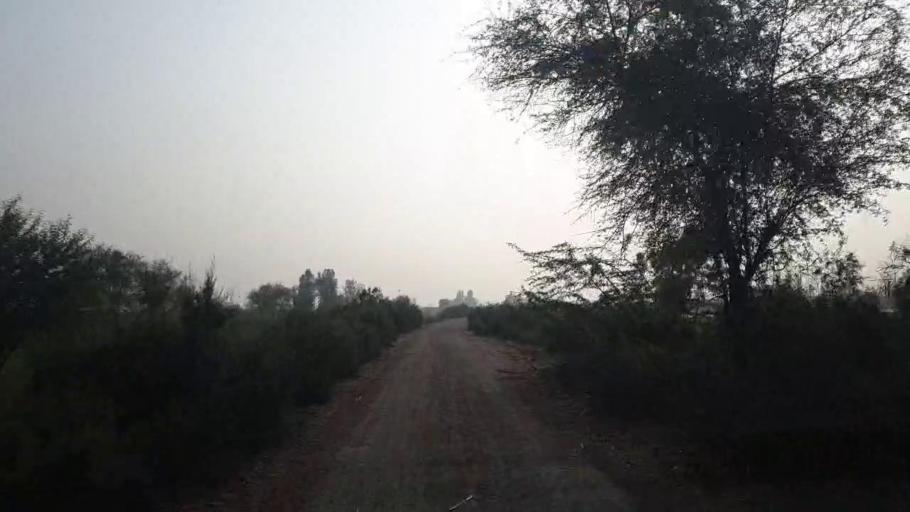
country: PK
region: Sindh
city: Shahdadpur
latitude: 25.8530
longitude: 68.5921
